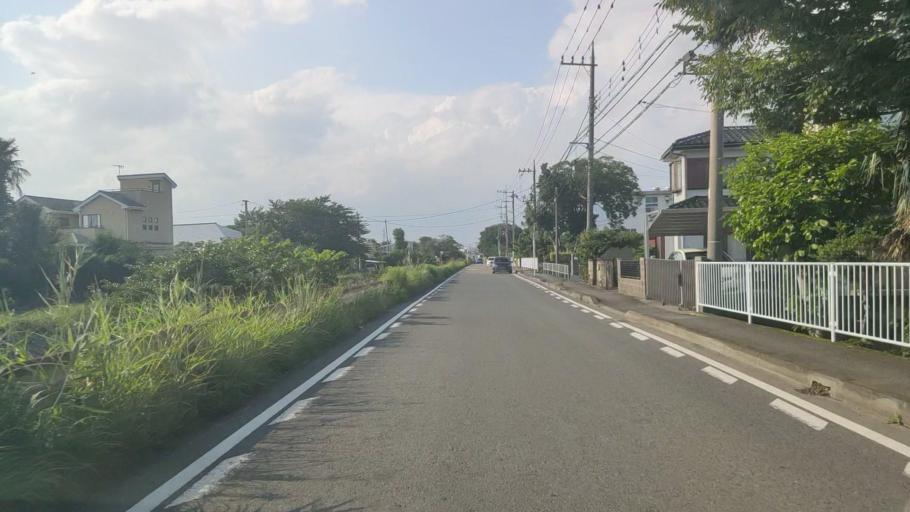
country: JP
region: Kanagawa
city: Isehara
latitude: 35.3870
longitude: 139.3386
